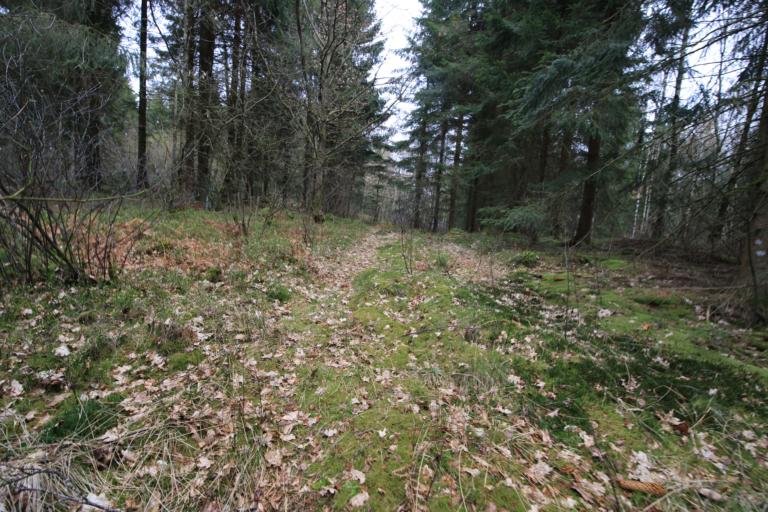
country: SE
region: Halland
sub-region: Varbergs Kommun
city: Tvaaker
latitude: 57.1506
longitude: 12.4567
